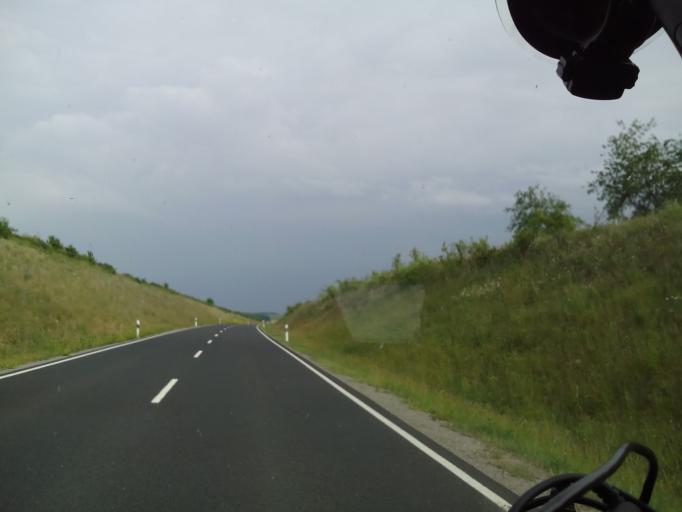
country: DE
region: Bavaria
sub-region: Regierungsbezirk Unterfranken
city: Mellrichstadt
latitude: 50.4400
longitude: 10.3183
